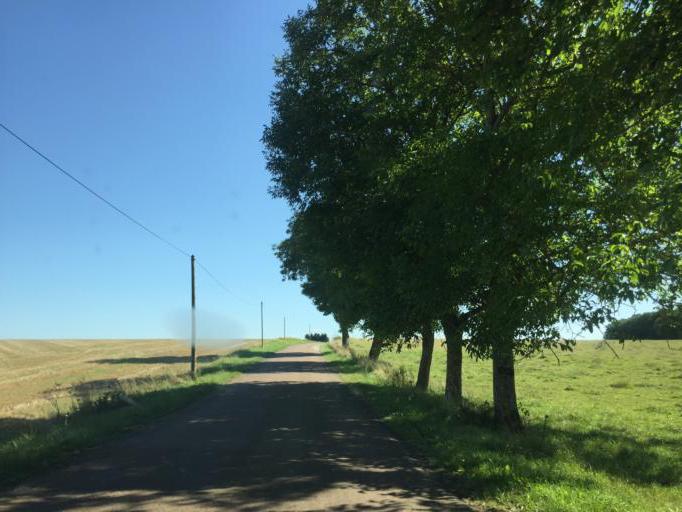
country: FR
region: Bourgogne
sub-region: Departement de l'Yonne
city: Fontenailles
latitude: 47.5246
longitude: 3.3477
